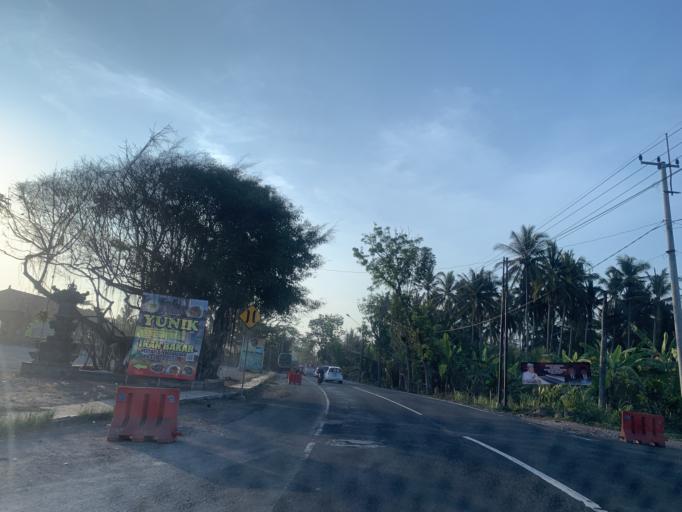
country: ID
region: Bali
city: Banjar Swastika
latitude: -8.4598
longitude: 114.9056
